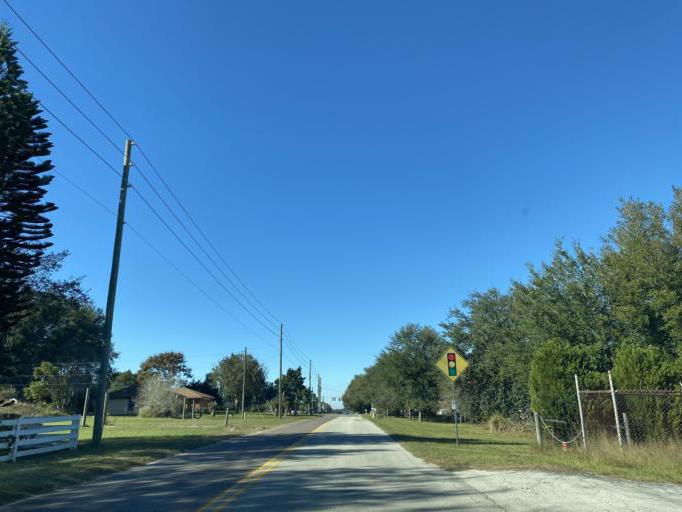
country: US
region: Florida
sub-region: Lake County
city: Minneola
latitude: 28.5251
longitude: -81.7046
